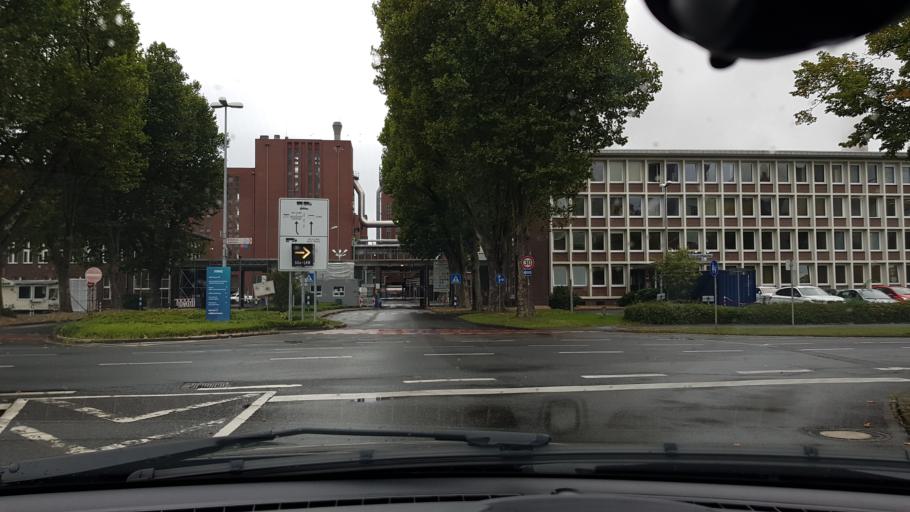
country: DE
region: North Rhine-Westphalia
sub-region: Regierungsbezirk Koln
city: Bergheim
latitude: 50.9887
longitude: 6.6632
